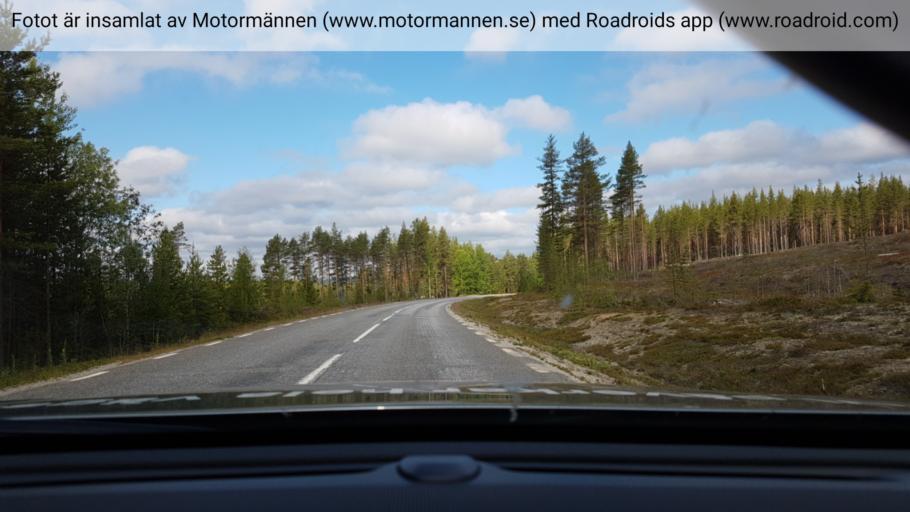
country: SE
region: Vaesterbotten
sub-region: Lycksele Kommun
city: Lycksele
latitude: 64.7799
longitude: 19.0035
